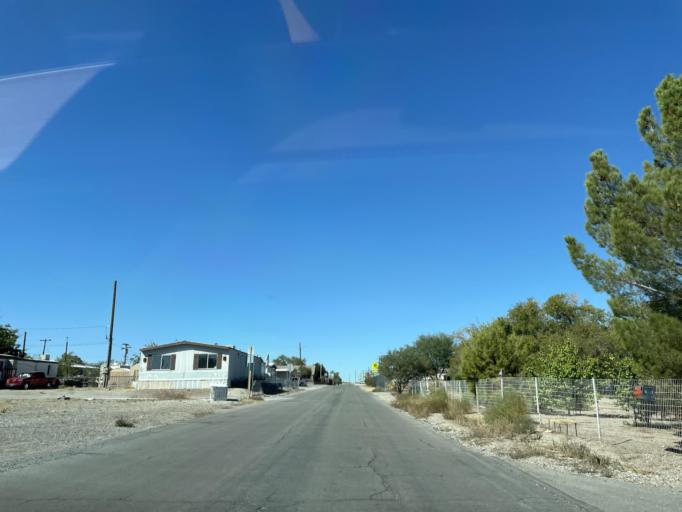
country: US
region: Nevada
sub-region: Nye County
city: Pahrump
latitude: 36.5734
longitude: -115.6734
